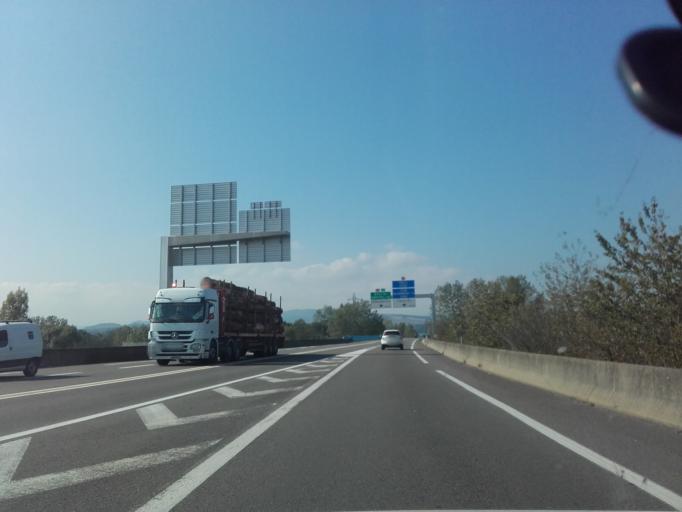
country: FR
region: Bourgogne
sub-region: Departement de Saone-et-Loire
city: Charnay-les-Macon
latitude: 46.2775
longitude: 4.8038
